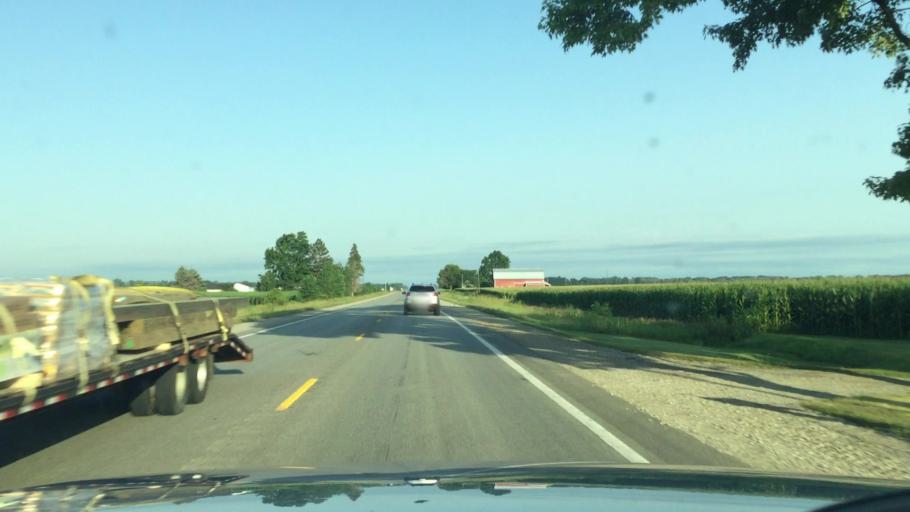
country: US
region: Michigan
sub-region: Montcalm County
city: Carson City
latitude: 43.1764
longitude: -84.7659
